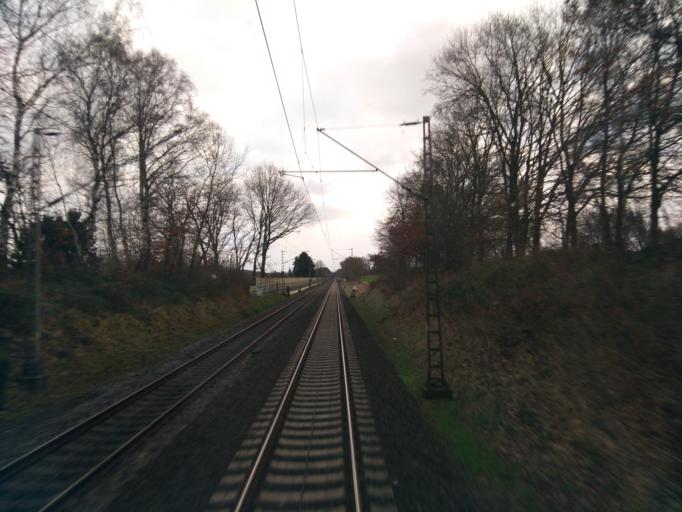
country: DE
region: Lower Saxony
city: Jelmstorf
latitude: 53.1033
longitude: 10.5468
